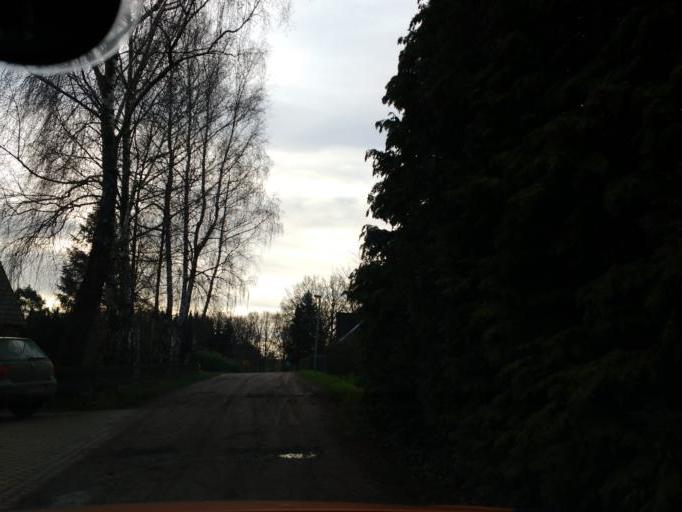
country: DE
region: Lower Saxony
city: Hude
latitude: 53.0945
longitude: 8.4565
